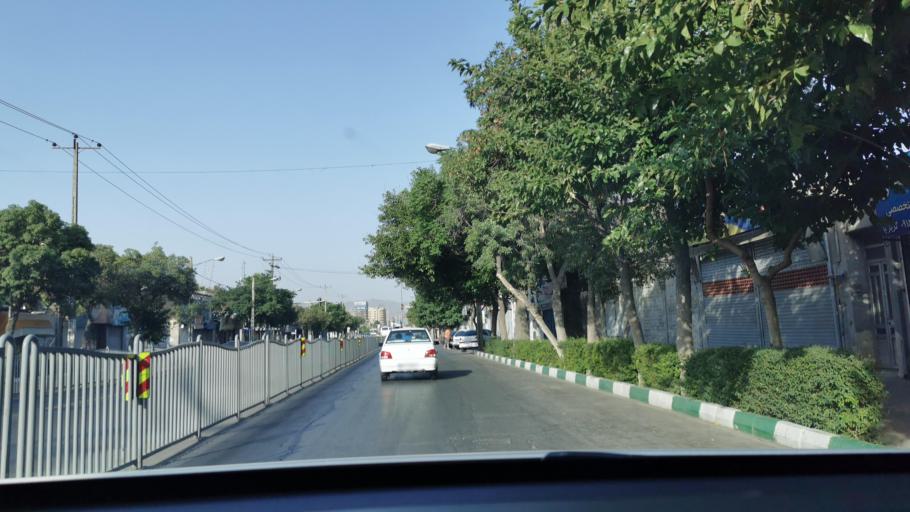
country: IR
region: Razavi Khorasan
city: Mashhad
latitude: 36.3007
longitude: 59.6359
